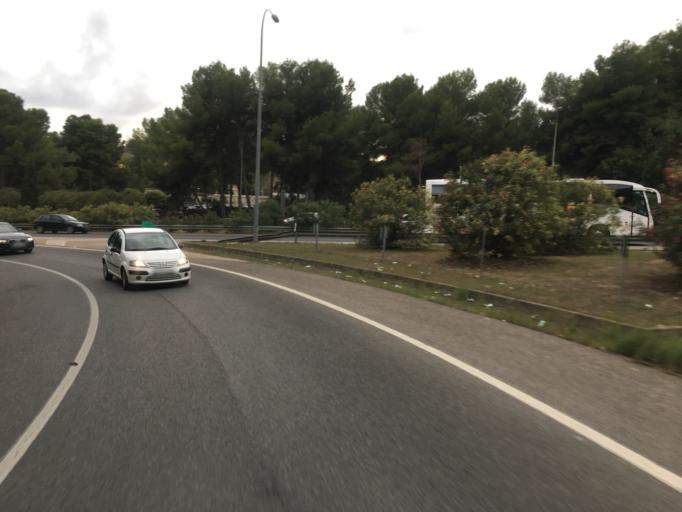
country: ES
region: Balearic Islands
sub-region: Illes Balears
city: Palma
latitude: 39.5540
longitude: 2.6156
